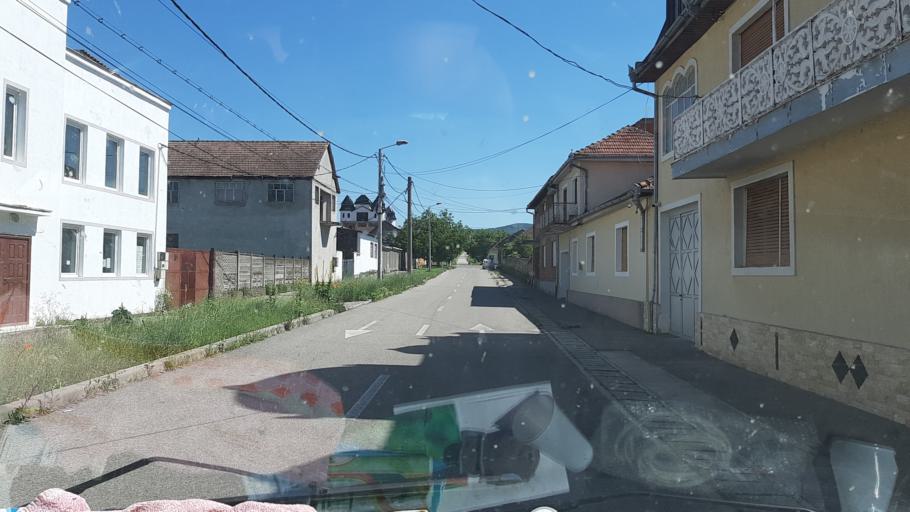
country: RO
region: Caras-Severin
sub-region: Oras Bocsa
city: Bocsa
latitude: 45.3773
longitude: 21.7155
